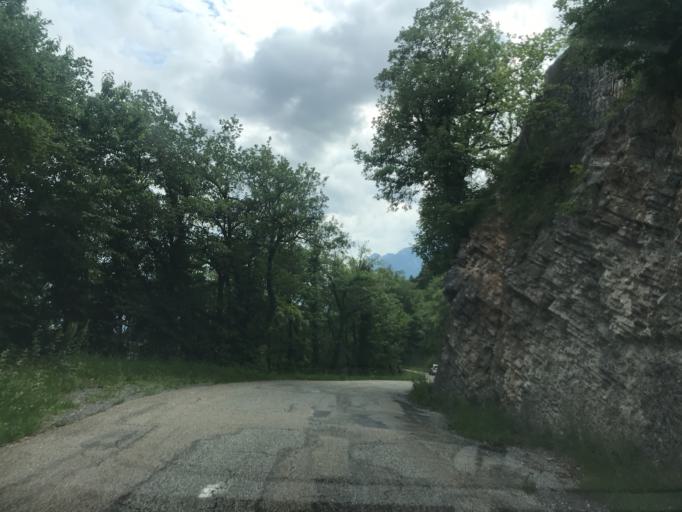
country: FR
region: Rhone-Alpes
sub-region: Departement de la Savoie
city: Mercury
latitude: 45.6808
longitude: 6.3333
